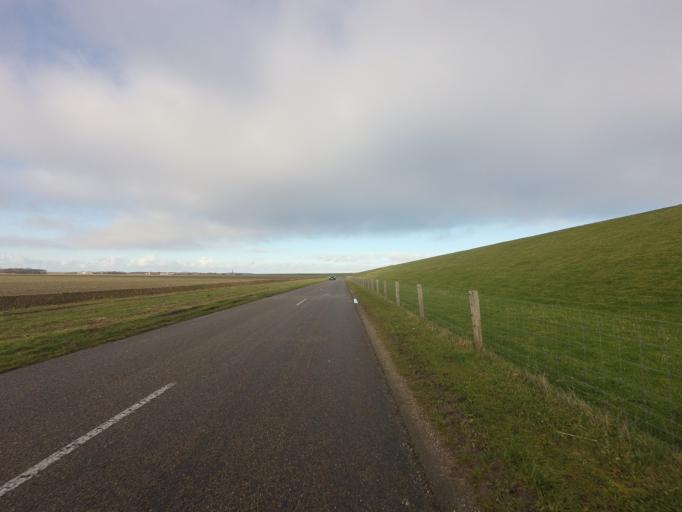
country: NL
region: North Holland
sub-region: Gemeente Texel
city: Den Burg
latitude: 53.1597
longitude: 4.8763
